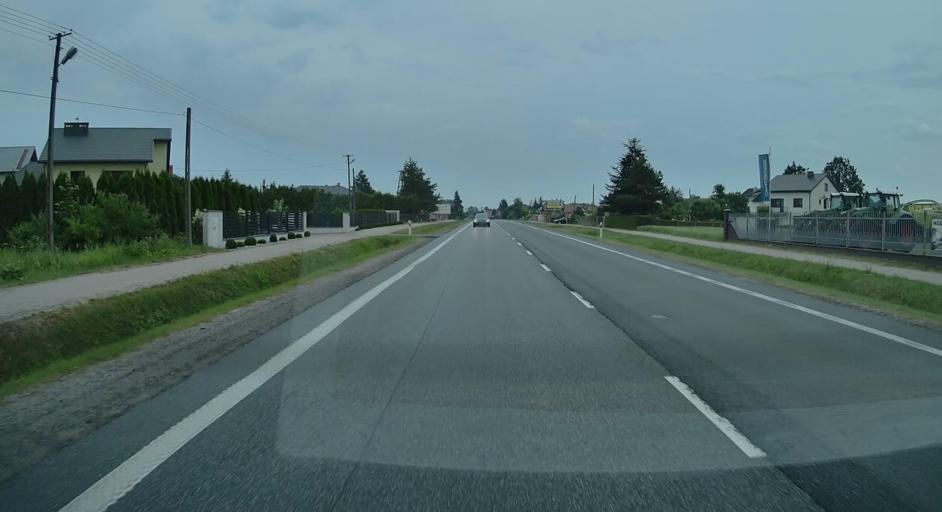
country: PL
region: Masovian Voivodeship
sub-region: Powiat siedlecki
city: Zbuczyn
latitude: 52.0920
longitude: 22.4253
